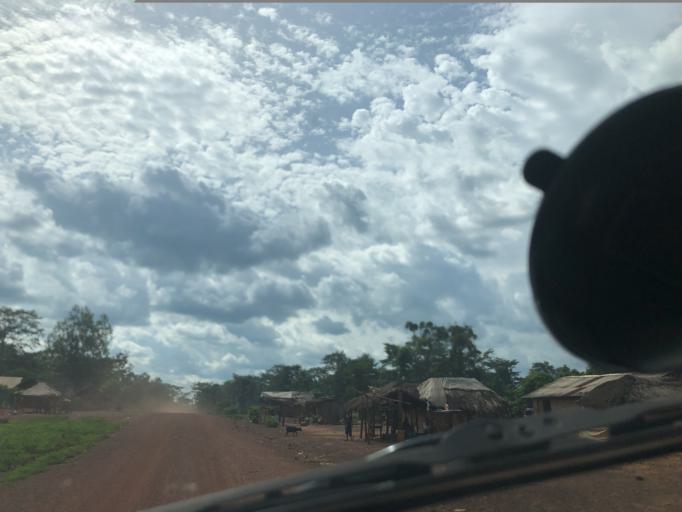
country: CF
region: Bangui
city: Bangui
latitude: 4.1768
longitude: 18.7564
